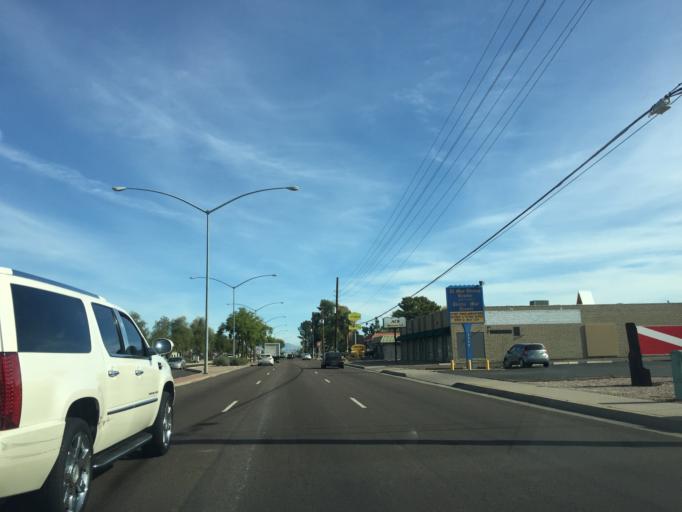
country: US
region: Arizona
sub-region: Maricopa County
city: Tempe
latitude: 33.4075
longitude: -111.8808
